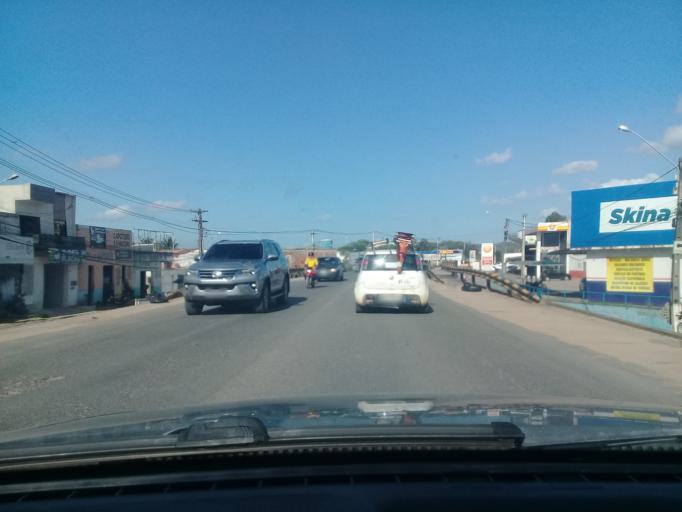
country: BR
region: Pernambuco
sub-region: Vitoria De Santo Antao
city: Vitoria de Santo Antao
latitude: -8.1121
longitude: -35.2904
